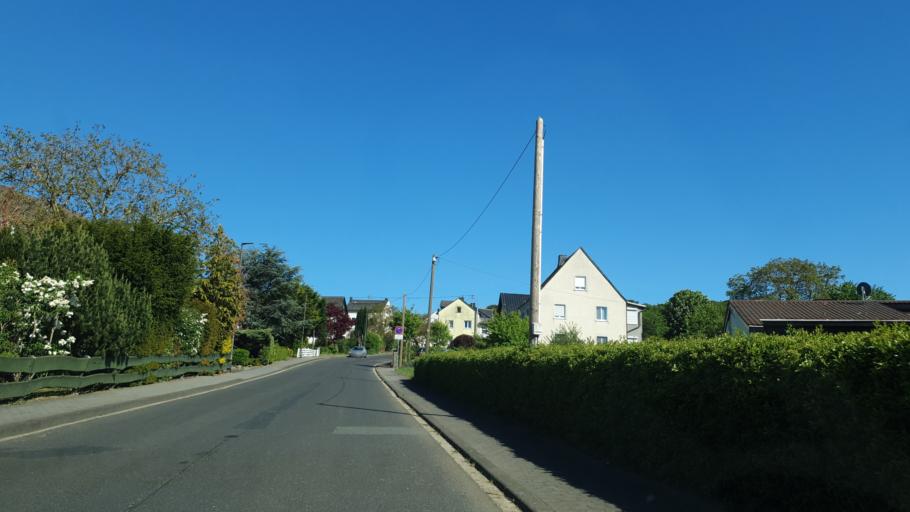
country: DE
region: Rheinland-Pfalz
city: Frucht
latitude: 50.3130
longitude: 7.6745
